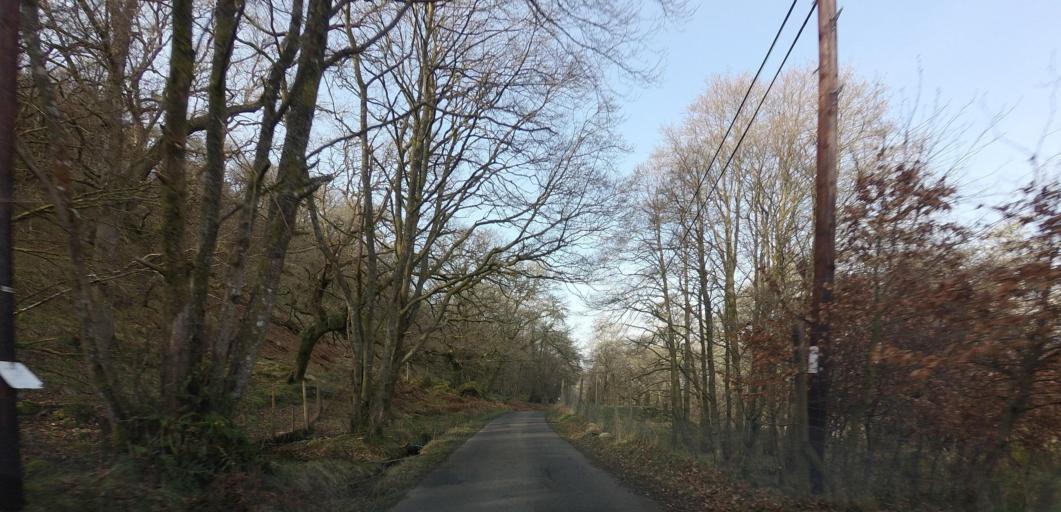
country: GB
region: Scotland
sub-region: Stirling
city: Callander
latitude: 56.4857
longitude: -4.2236
